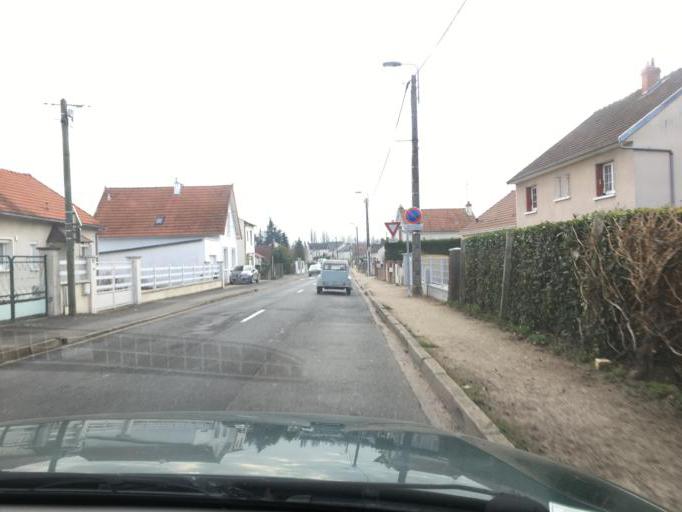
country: FR
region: Centre
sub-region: Departement du Loiret
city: Saran
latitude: 47.9485
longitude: 1.8818
